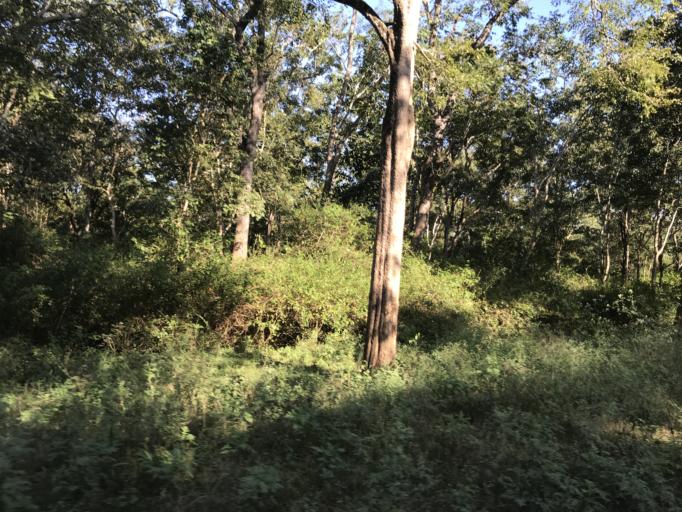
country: IN
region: Karnataka
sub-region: Mysore
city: Heggadadevankote
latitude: 11.9717
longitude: 76.2434
